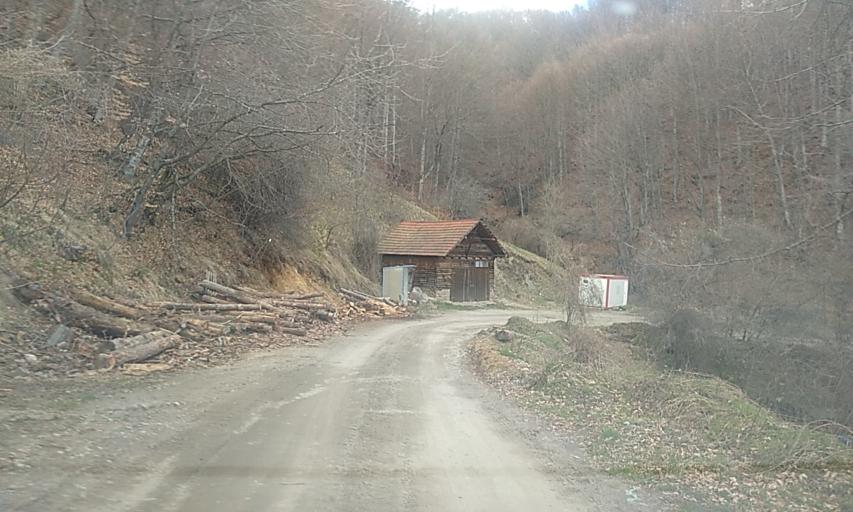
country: RS
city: Radovnica
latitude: 42.3475
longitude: 22.3428
